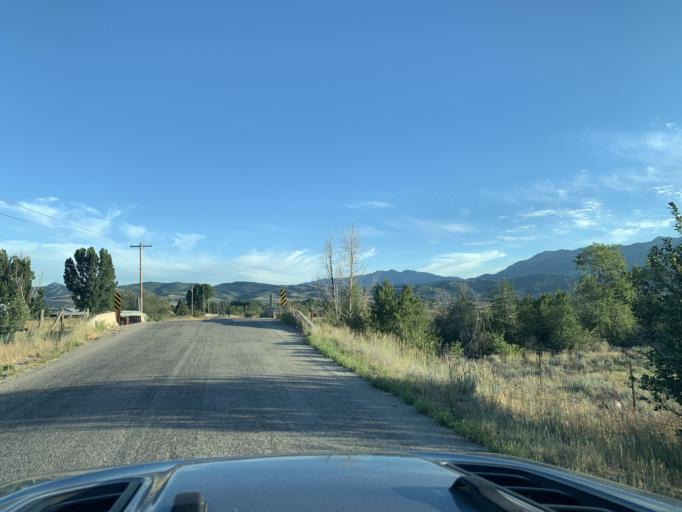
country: US
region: Utah
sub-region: Weber County
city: Wolf Creek
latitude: 41.2912
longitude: -111.7580
